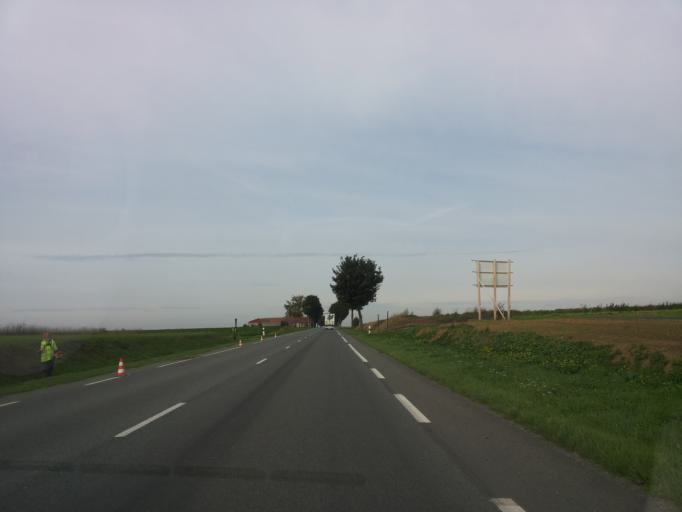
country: FR
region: Nord-Pas-de-Calais
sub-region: Departement du Pas-de-Calais
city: Marquion
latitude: 50.2169
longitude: 3.0638
